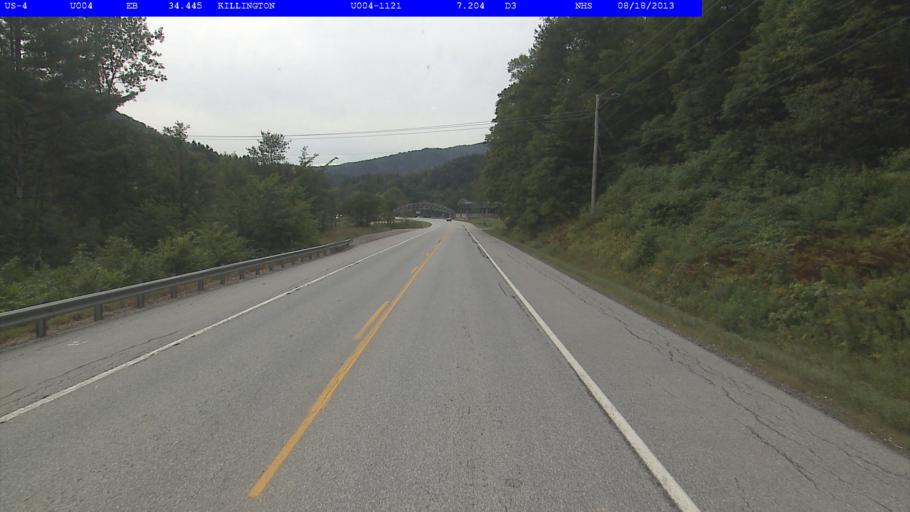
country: US
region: Vermont
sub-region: Rutland County
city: Rutland
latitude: 43.6173
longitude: -72.7580
